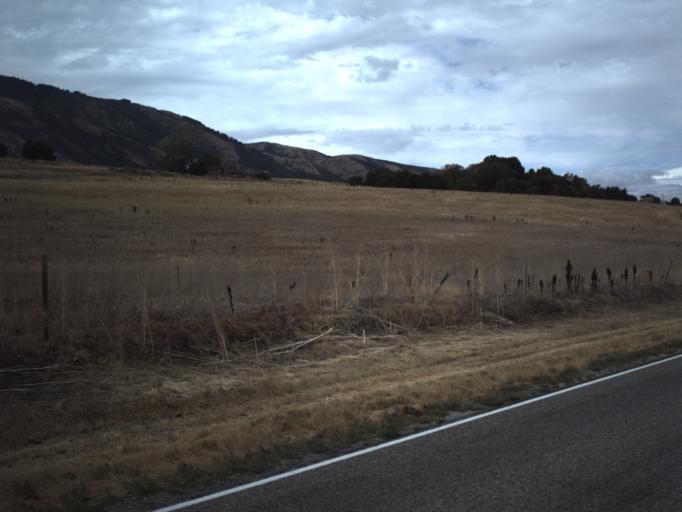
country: US
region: Utah
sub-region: Cache County
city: Mendon
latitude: 41.6935
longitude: -111.9714
